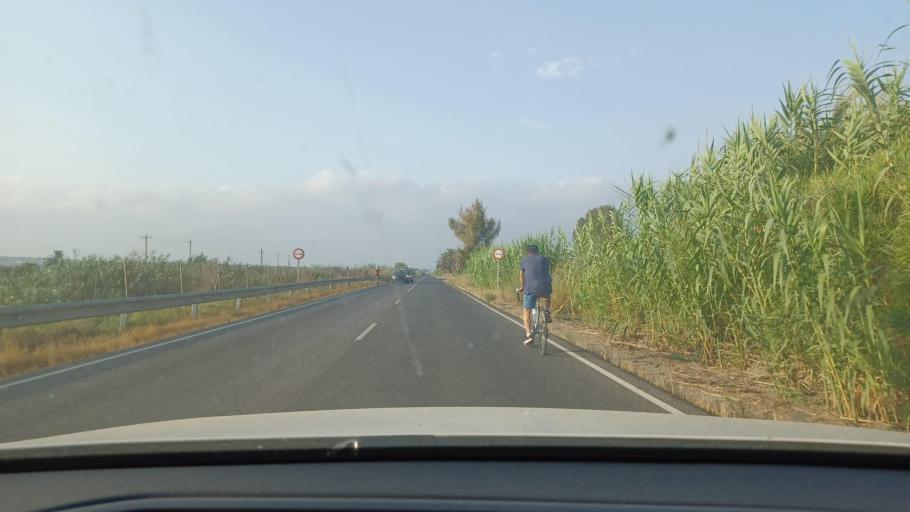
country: ES
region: Valencia
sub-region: Provincia de Alicante
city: Daya Vieja
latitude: 38.1679
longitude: -0.7025
